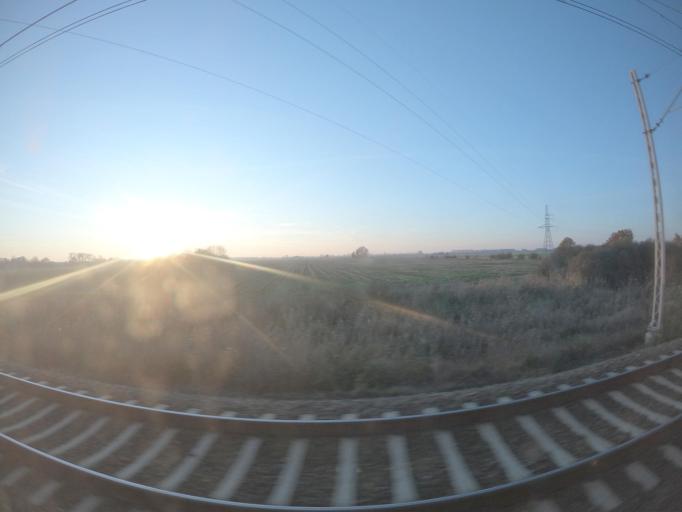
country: PL
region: Lubusz
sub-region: Powiat gorzowski
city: Kostrzyn nad Odra
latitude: 52.5480
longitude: 14.6511
